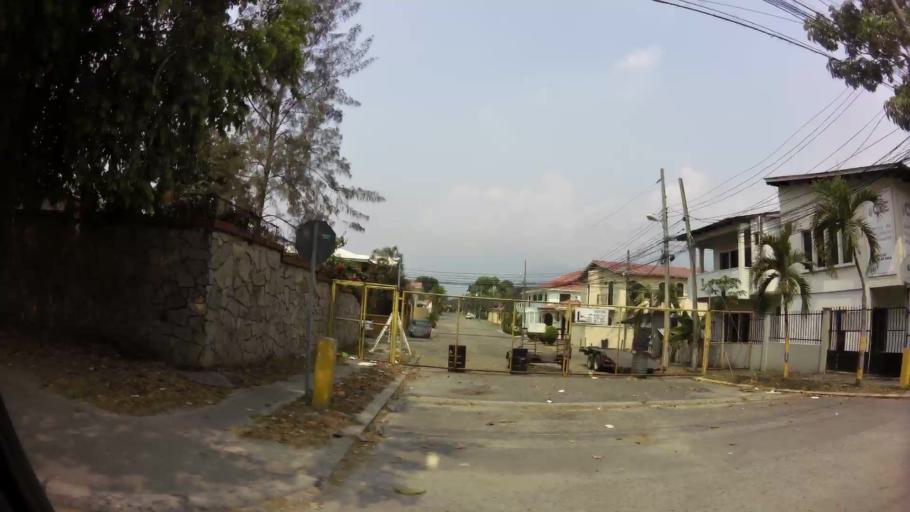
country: HN
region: Cortes
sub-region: San Pedro Sula
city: Pena Blanca
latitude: 15.5495
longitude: -88.0106
